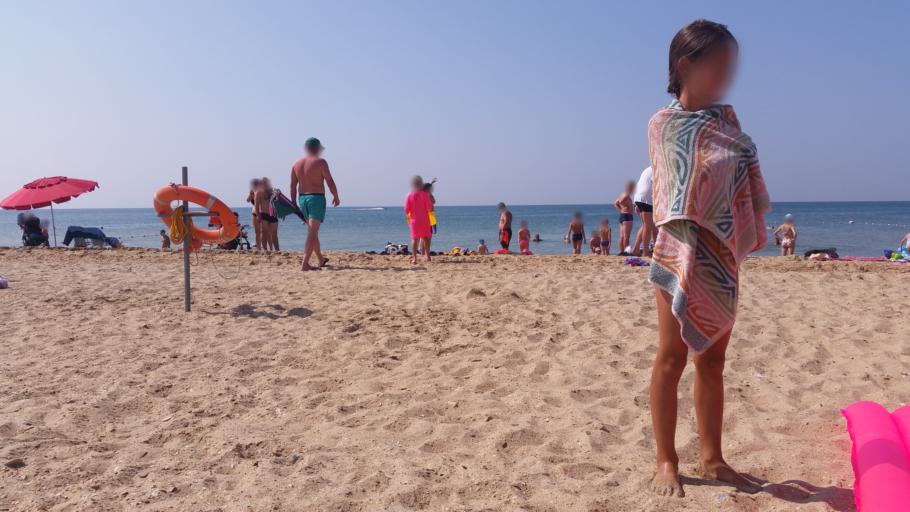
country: RU
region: Krasnodarskiy
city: Blagovetschenskaya
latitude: 45.0638
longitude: 37.0438
